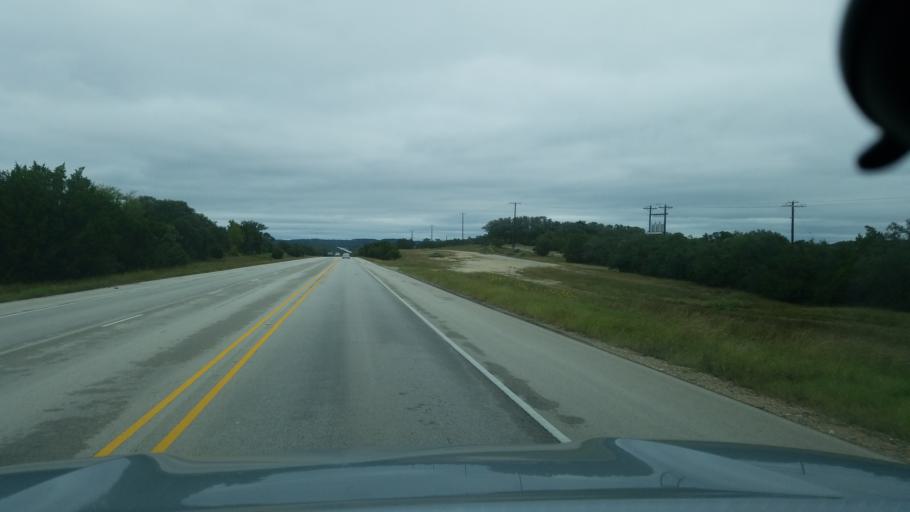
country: US
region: Texas
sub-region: Blanco County
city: Blanco
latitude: 29.9821
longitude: -98.4090
